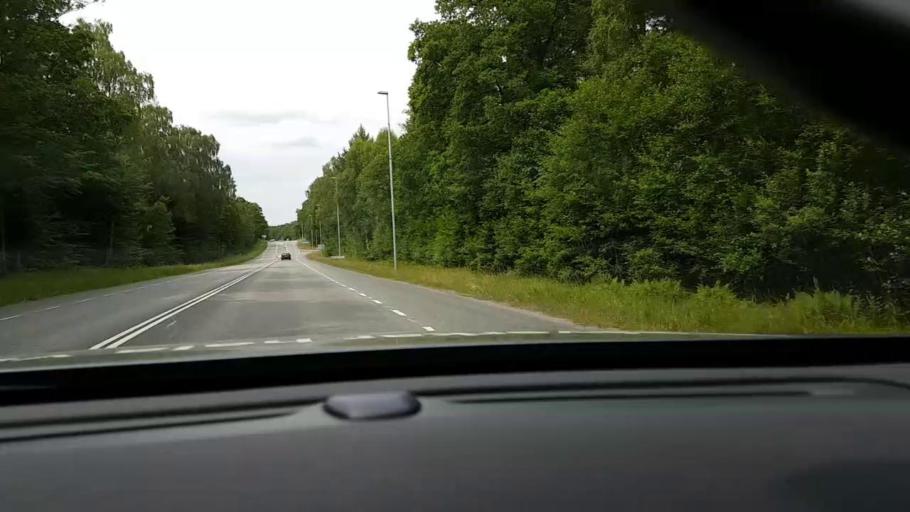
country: SE
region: Skane
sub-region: Hassleholms Kommun
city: Hassleholm
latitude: 56.1615
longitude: 13.7381
